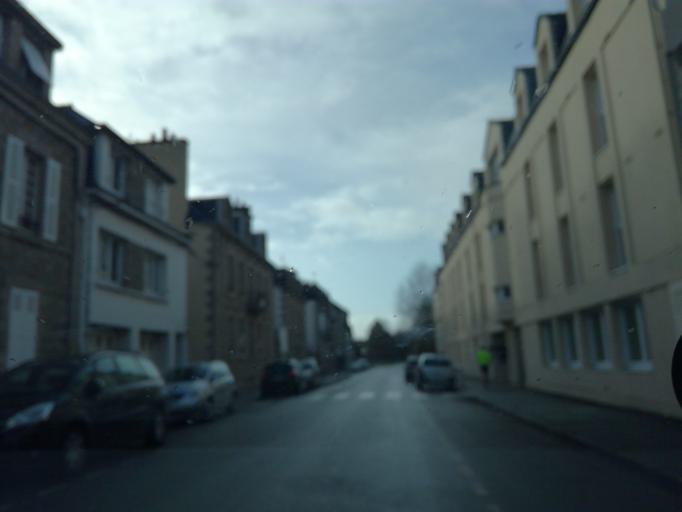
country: FR
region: Brittany
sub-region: Departement du Morbihan
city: Pontivy
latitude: 48.0608
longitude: -2.9676
